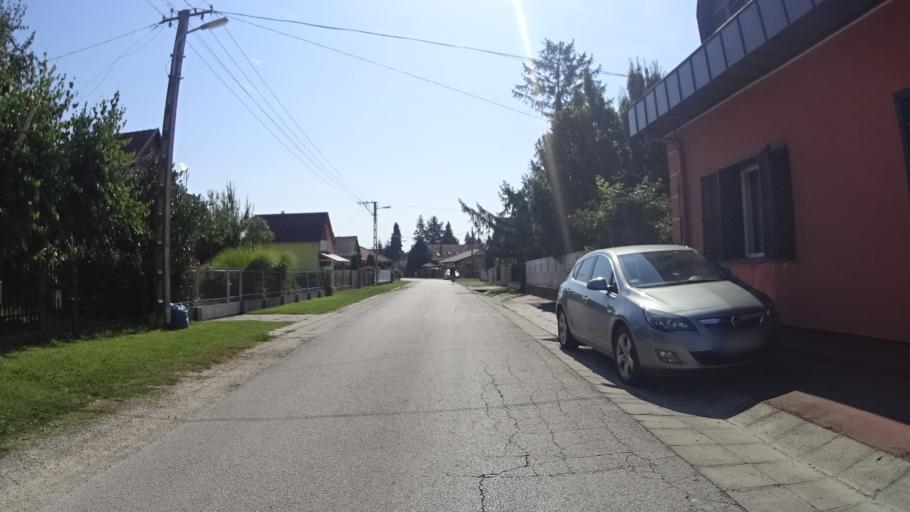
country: HU
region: Somogy
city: Balatonbereny
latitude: 46.7060
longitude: 17.3662
